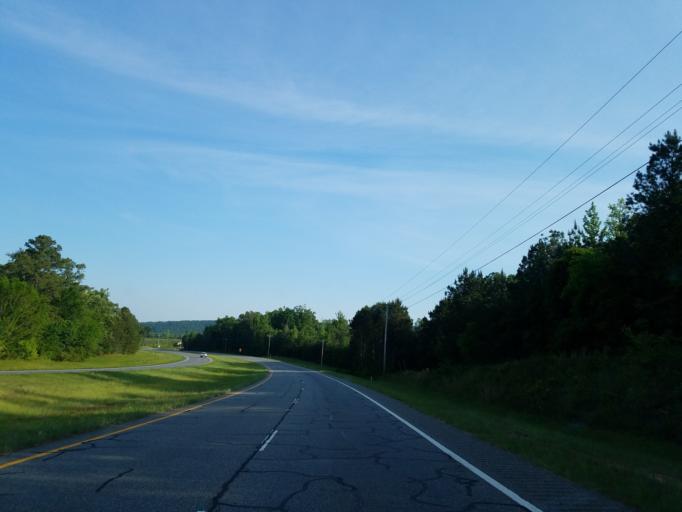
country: US
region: Georgia
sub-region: Chattooga County
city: Summerville
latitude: 34.4283
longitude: -85.2497
